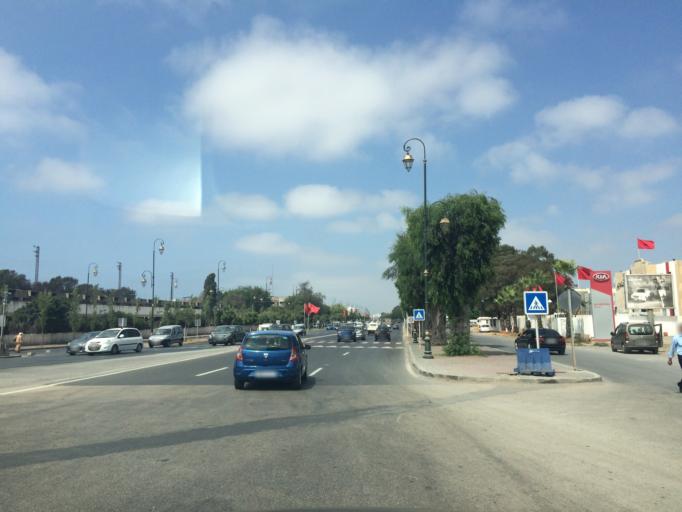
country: MA
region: Rabat-Sale-Zemmour-Zaer
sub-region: Skhirate-Temara
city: Temara
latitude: 33.9762
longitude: -6.8772
